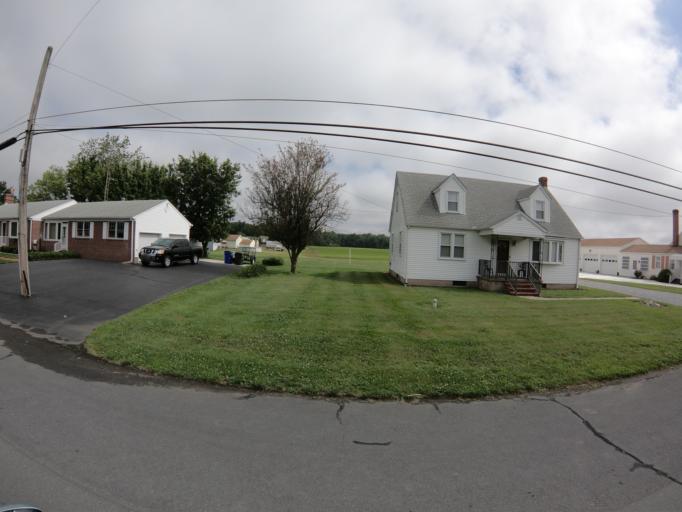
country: US
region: Delaware
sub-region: Kent County
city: Felton
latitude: 39.0063
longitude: -75.5668
